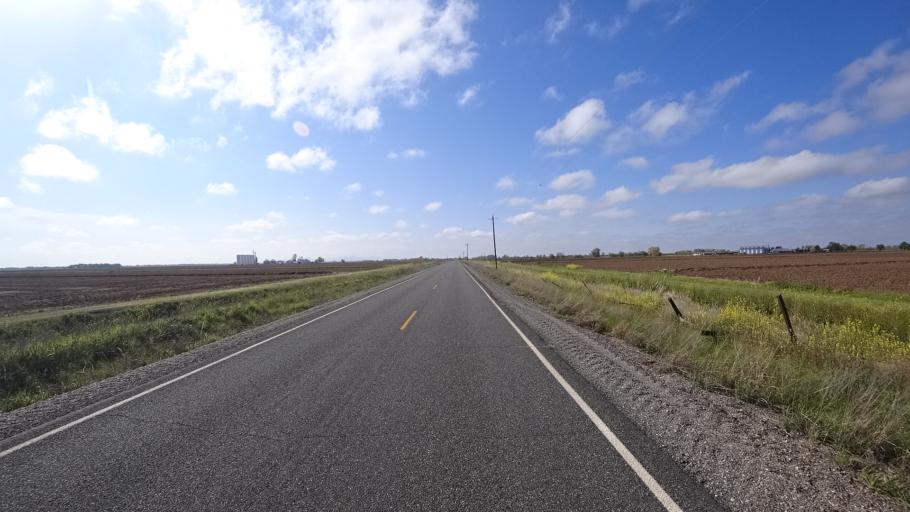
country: US
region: California
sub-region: Butte County
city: Durham
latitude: 39.5025
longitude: -121.9299
